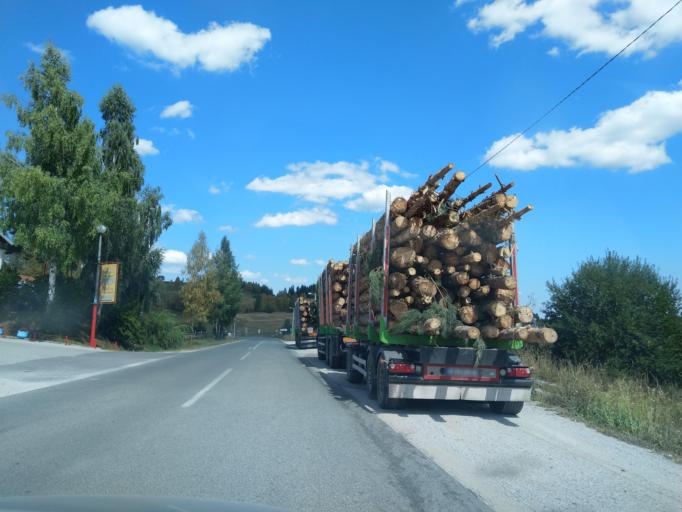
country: RS
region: Central Serbia
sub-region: Zlatiborski Okrug
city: Nova Varos
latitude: 43.4258
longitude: 19.8288
